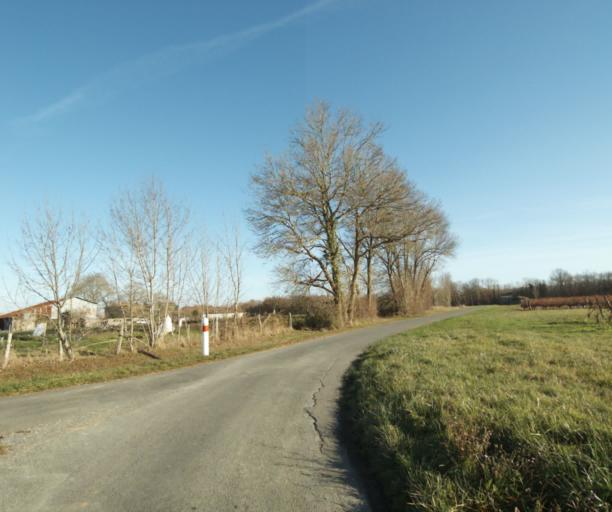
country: FR
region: Poitou-Charentes
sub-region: Departement de la Charente-Maritime
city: Burie
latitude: 45.7773
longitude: -0.4427
